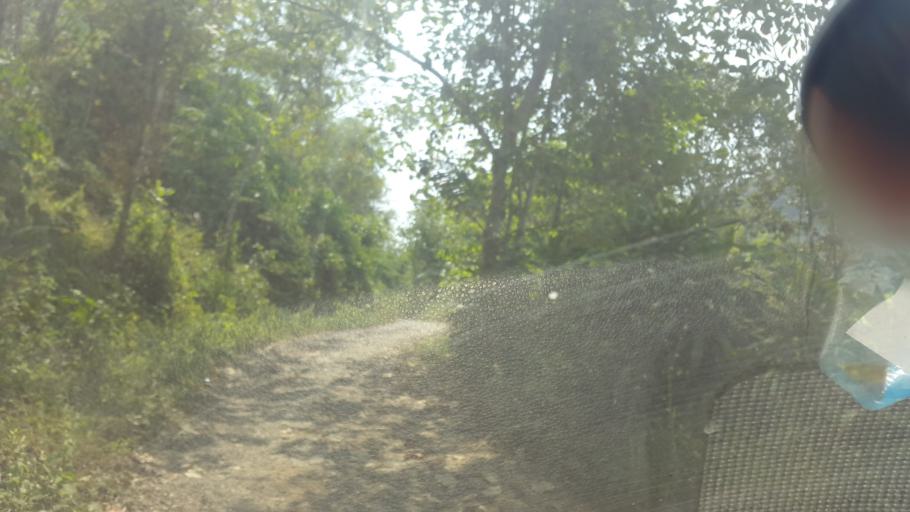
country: ID
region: West Java
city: Sindangsari
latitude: -6.9512
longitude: 106.6696
